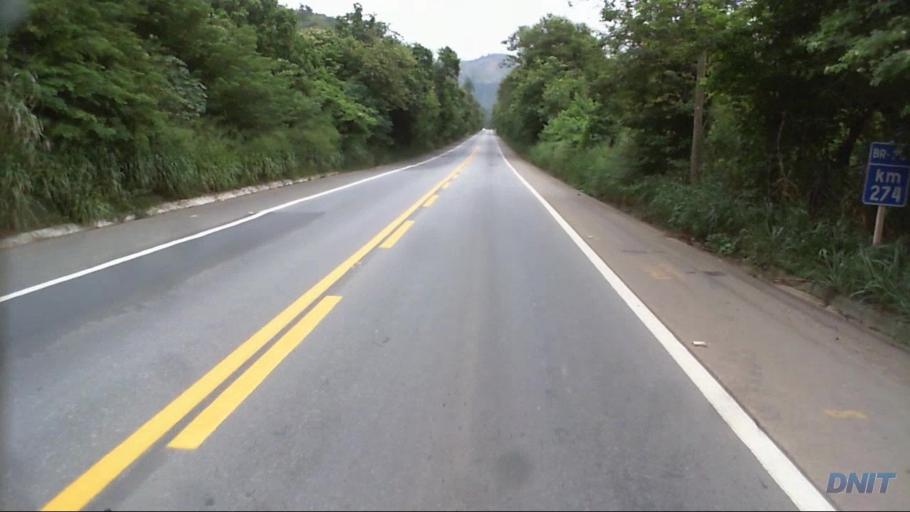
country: BR
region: Minas Gerais
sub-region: Timoteo
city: Timoteo
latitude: -19.5497
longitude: -42.7020
